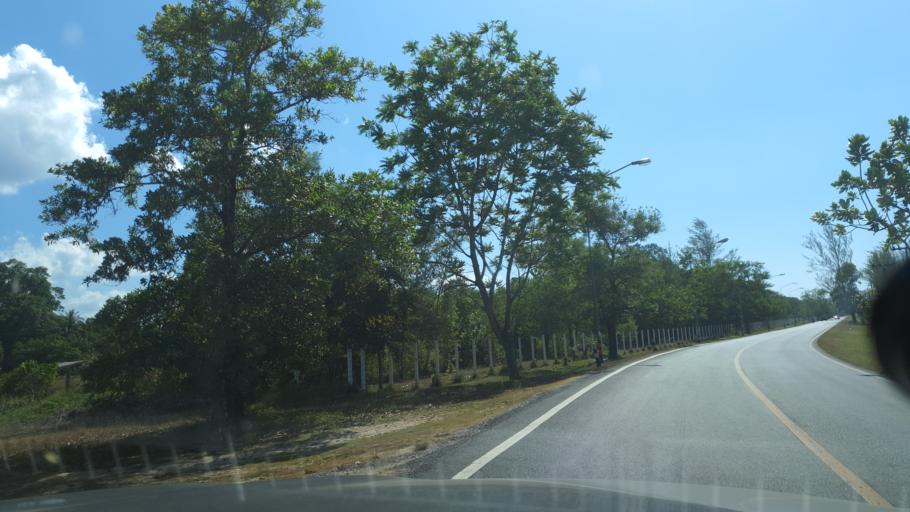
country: TH
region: Phangnga
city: Ban Khao Lak
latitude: 8.5821
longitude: 98.2464
